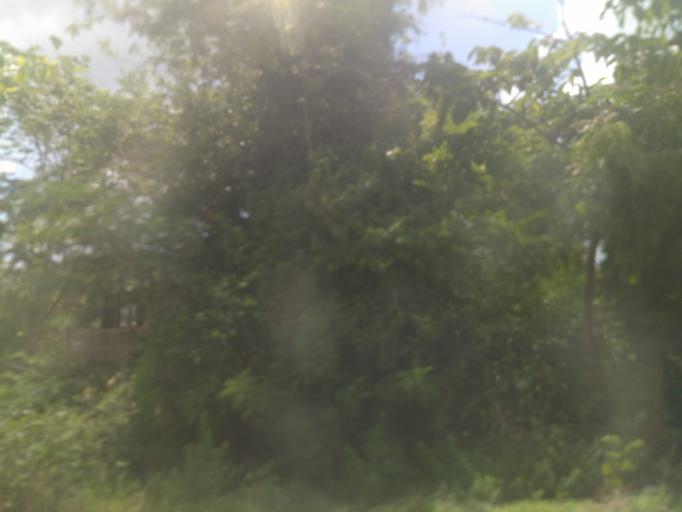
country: TZ
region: Zanzibar Urban/West
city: Zanzibar
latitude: -6.2888
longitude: 39.2856
